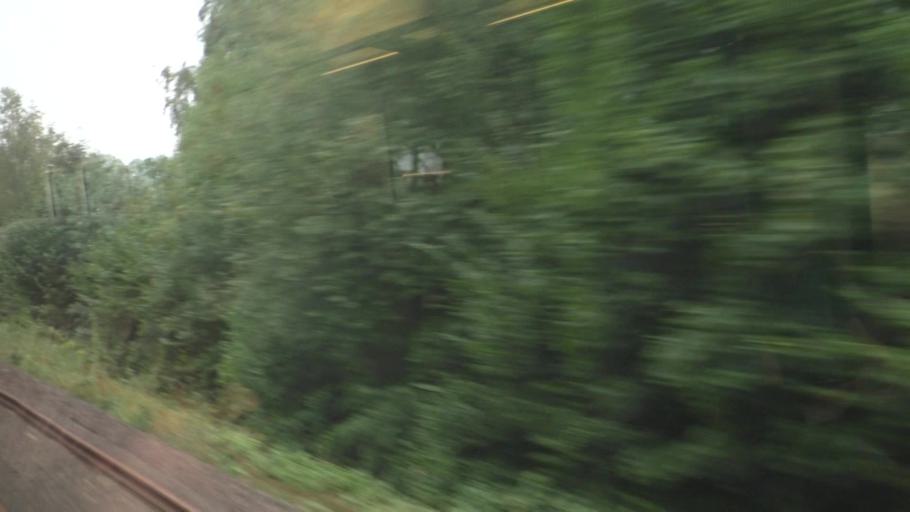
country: DE
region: Saxony
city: Arnsdorf
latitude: 51.1024
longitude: 13.9533
